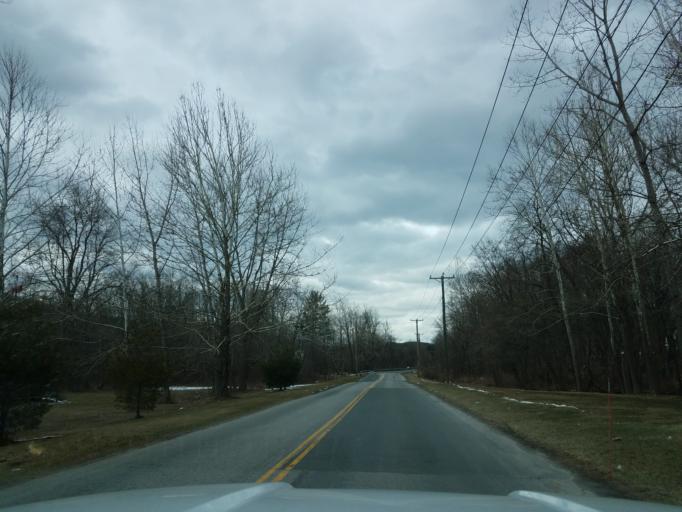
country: US
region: Connecticut
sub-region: Litchfield County
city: New Milford
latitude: 41.5869
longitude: -73.4248
